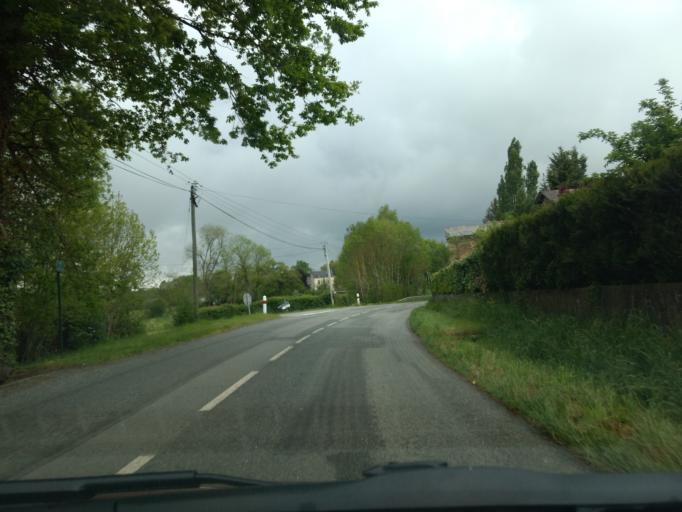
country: FR
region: Midi-Pyrenees
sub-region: Departement de l'Aveyron
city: Montbazens
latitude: 44.4838
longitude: 2.2240
